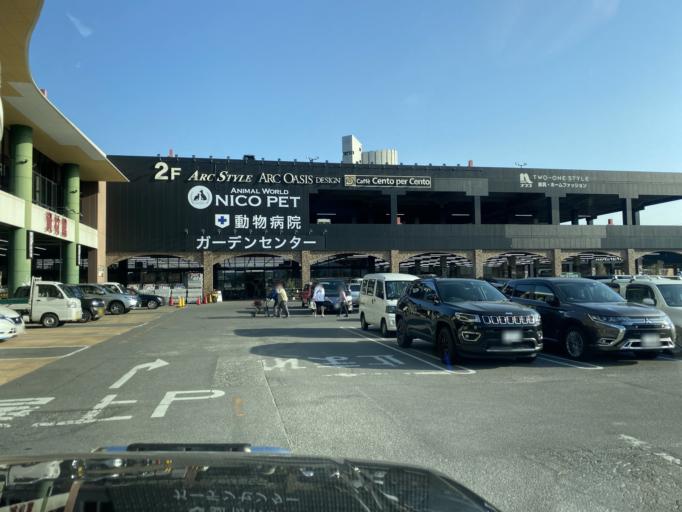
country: JP
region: Kyoto
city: Yawata
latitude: 34.8406
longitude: 135.7193
